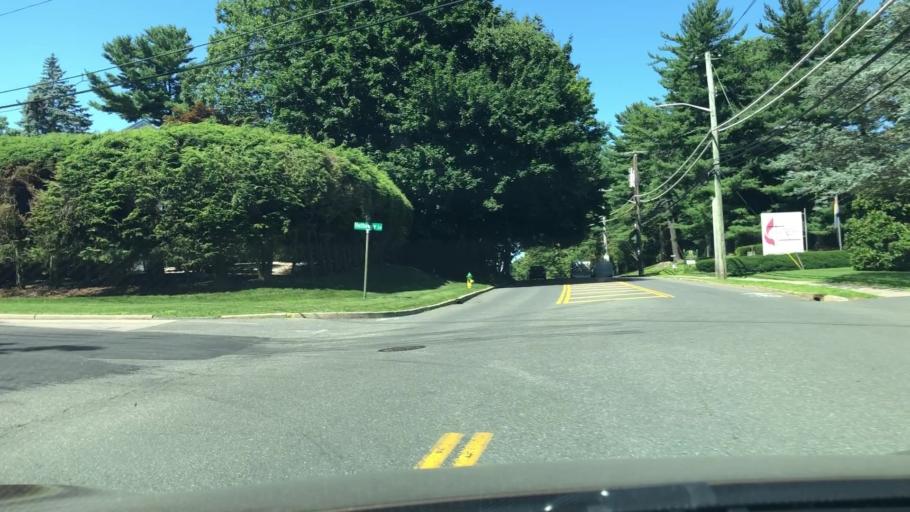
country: US
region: New York
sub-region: Westchester County
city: White Plains
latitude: 41.0215
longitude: -73.7460
